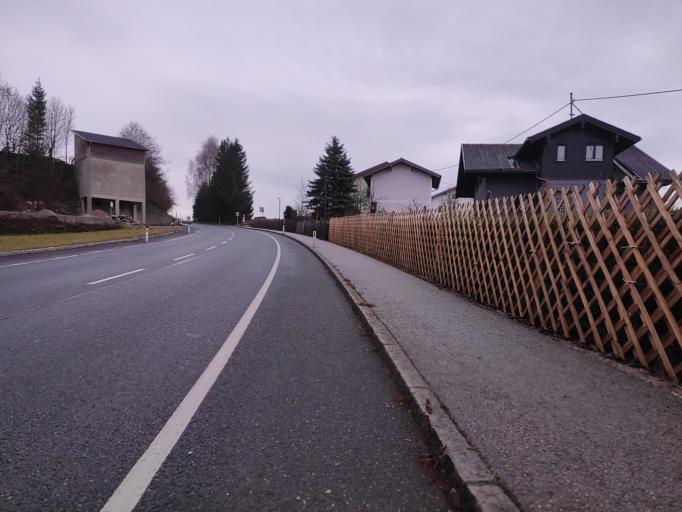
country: AT
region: Salzburg
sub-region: Politischer Bezirk Salzburg-Umgebung
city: Obertrum am See
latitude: 47.9281
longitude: 13.0895
